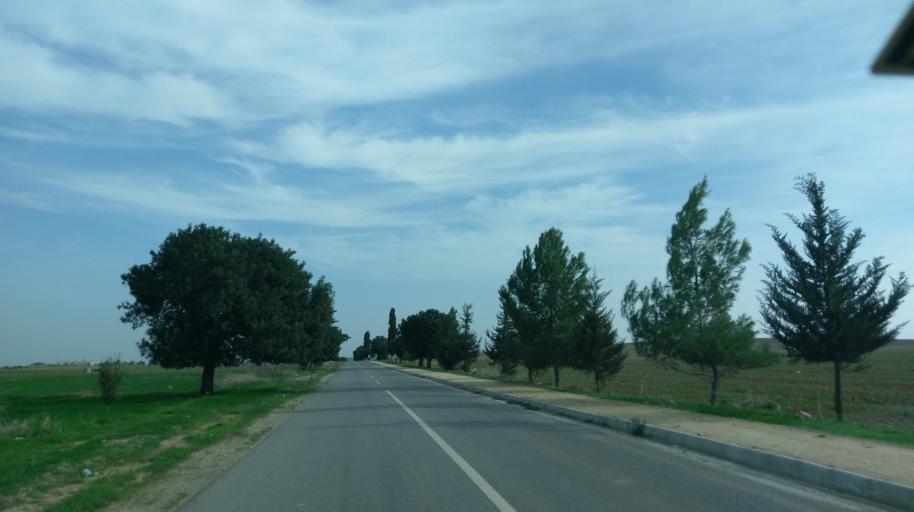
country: CY
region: Lefkosia
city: Mammari
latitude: 35.1975
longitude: 33.2355
